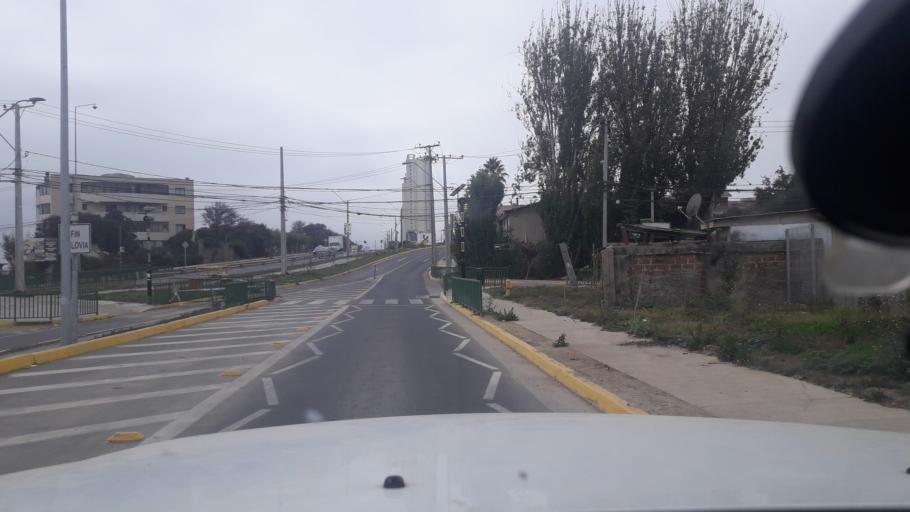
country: CL
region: Valparaiso
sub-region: Provincia de Valparaiso
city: Vina del Mar
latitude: -32.9340
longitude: -71.5257
